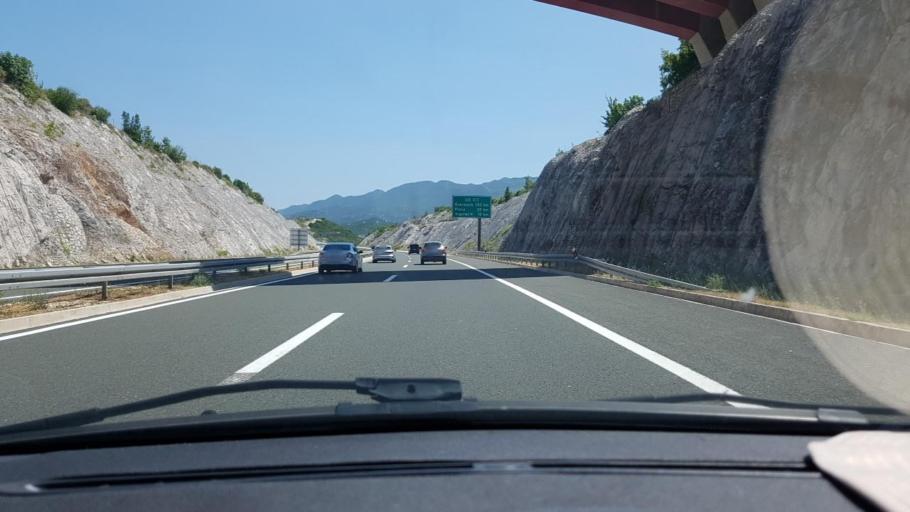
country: HR
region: Splitsko-Dalmatinska
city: Vrgorac
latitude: 43.2144
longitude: 17.2675
